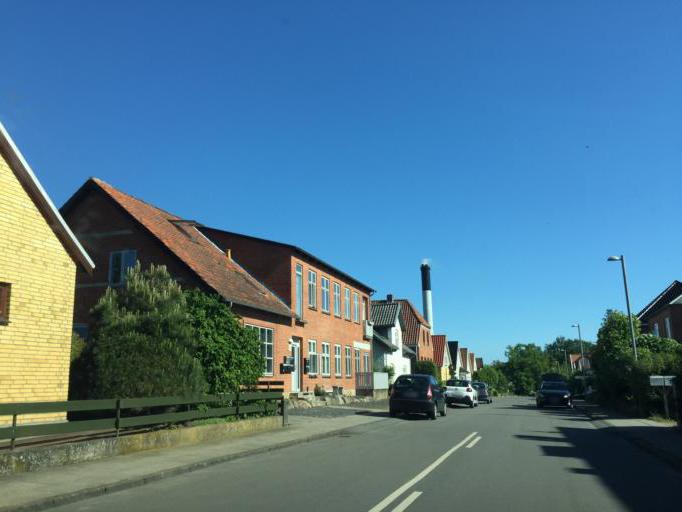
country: DK
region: South Denmark
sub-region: Odense Kommune
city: Odense
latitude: 55.3606
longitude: 10.3795
